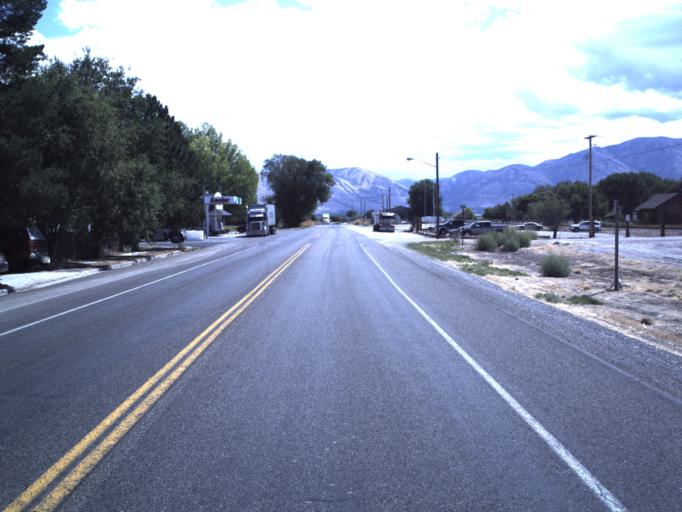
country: US
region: Utah
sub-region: Box Elder County
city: Honeyville
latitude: 41.5507
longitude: -112.1091
